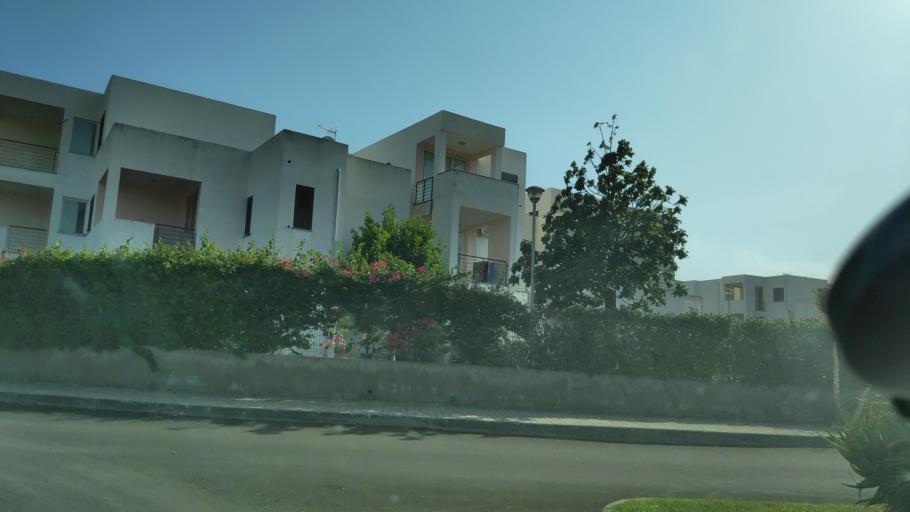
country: IT
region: Calabria
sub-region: Provincia di Catanzaro
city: Isca Marina
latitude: 38.6019
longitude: 16.5641
